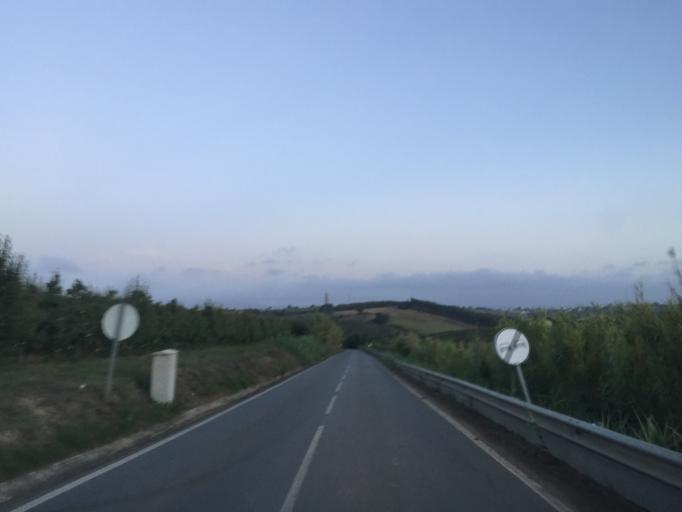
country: PT
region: Leiria
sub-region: Bombarral
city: Bombarral
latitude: 39.2751
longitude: -9.1732
